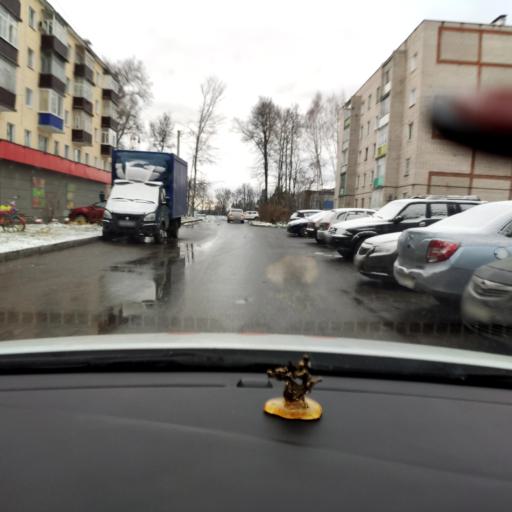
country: RU
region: Tatarstan
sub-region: Zelenodol'skiy Rayon
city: Zelenodolsk
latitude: 55.8455
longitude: 48.5072
